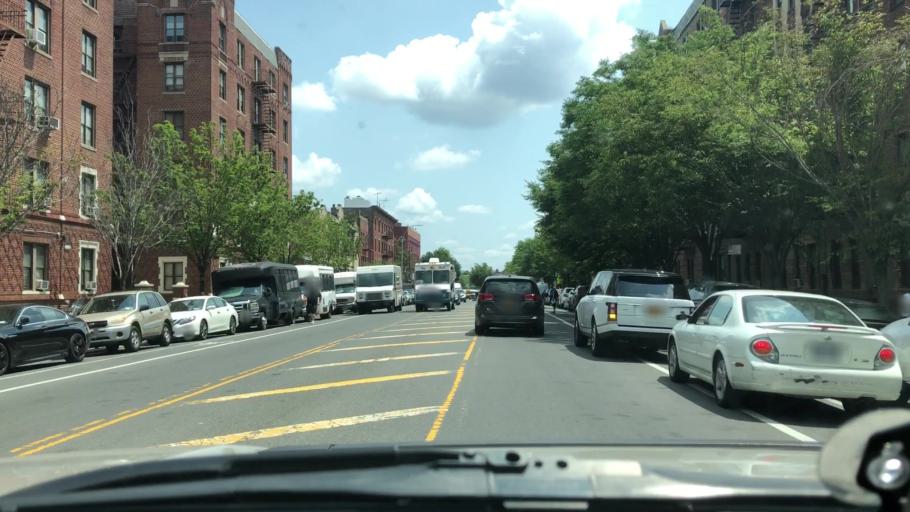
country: US
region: New York
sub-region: Kings County
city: Brooklyn
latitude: 40.6638
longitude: -73.9528
